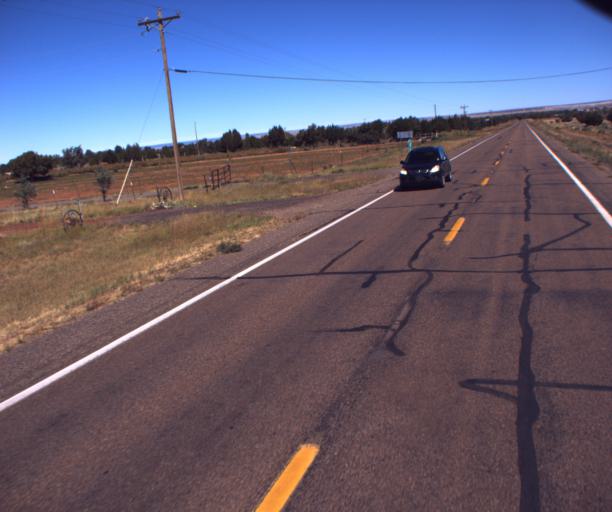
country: US
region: Arizona
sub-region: Apache County
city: Saint Johns
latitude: 34.4713
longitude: -109.3919
